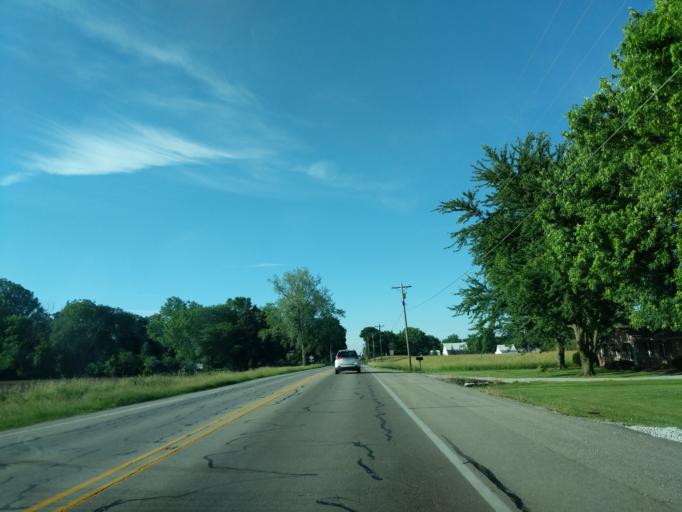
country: US
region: Indiana
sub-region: Hancock County
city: Greenfield
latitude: 39.8422
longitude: -85.7700
